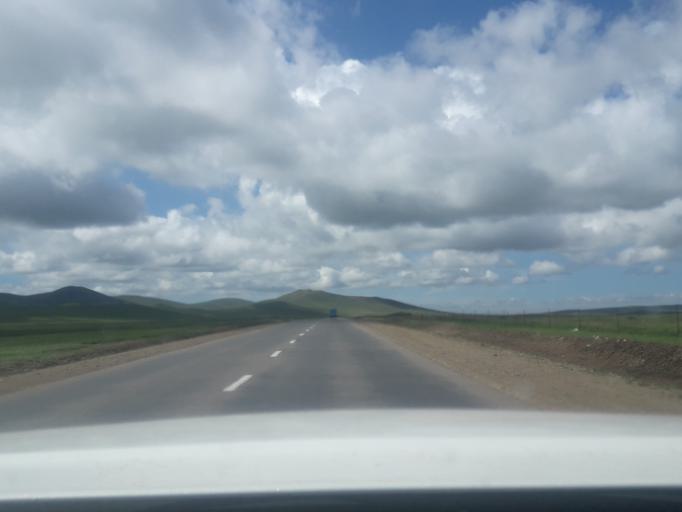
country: MN
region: Central Aimak
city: Altanbulag
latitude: 47.9002
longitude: 106.4555
